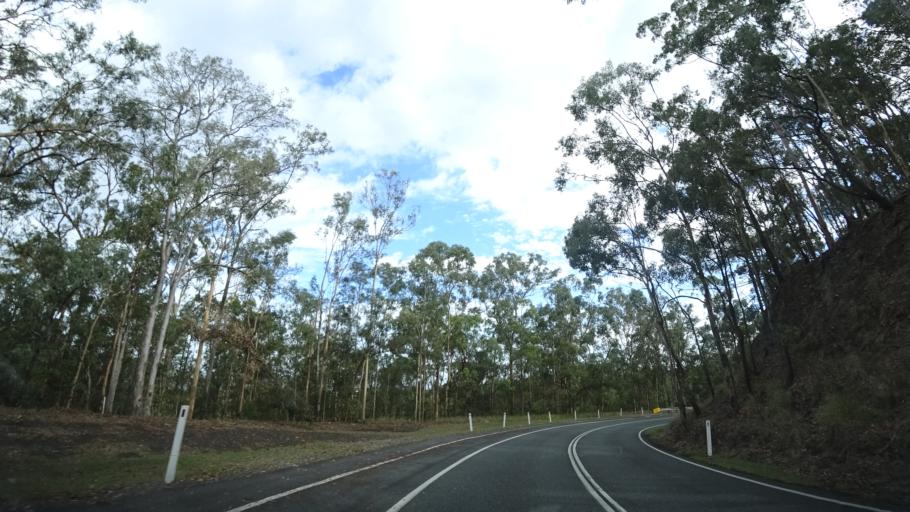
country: AU
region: Queensland
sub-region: Brisbane
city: Taringa
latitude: -27.4794
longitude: 152.9547
